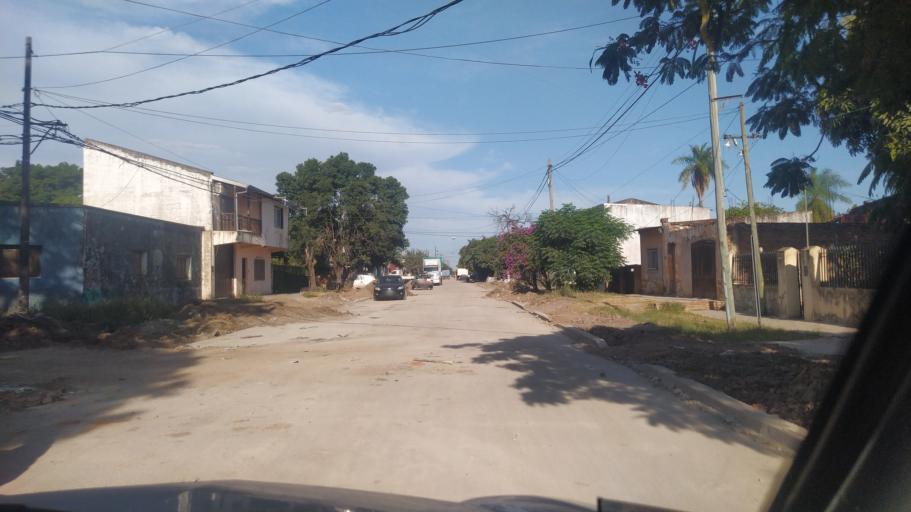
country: AR
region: Corrientes
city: Corrientes
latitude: -27.4799
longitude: -58.8128
